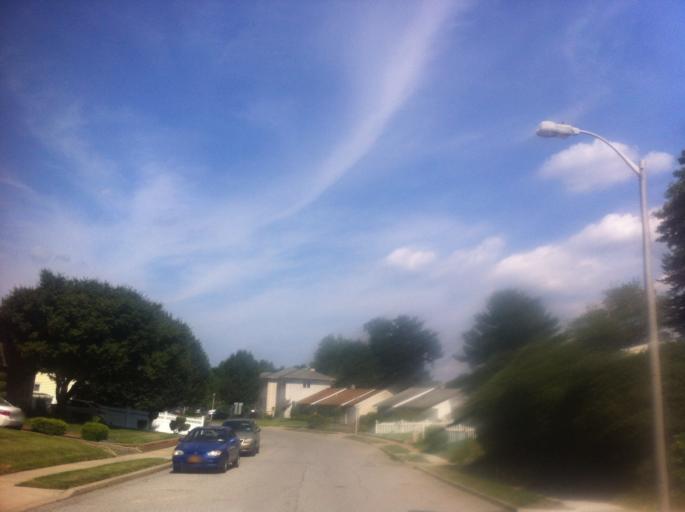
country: US
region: New York
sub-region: Nassau County
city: Locust Valley
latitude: 40.8563
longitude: -73.6049
